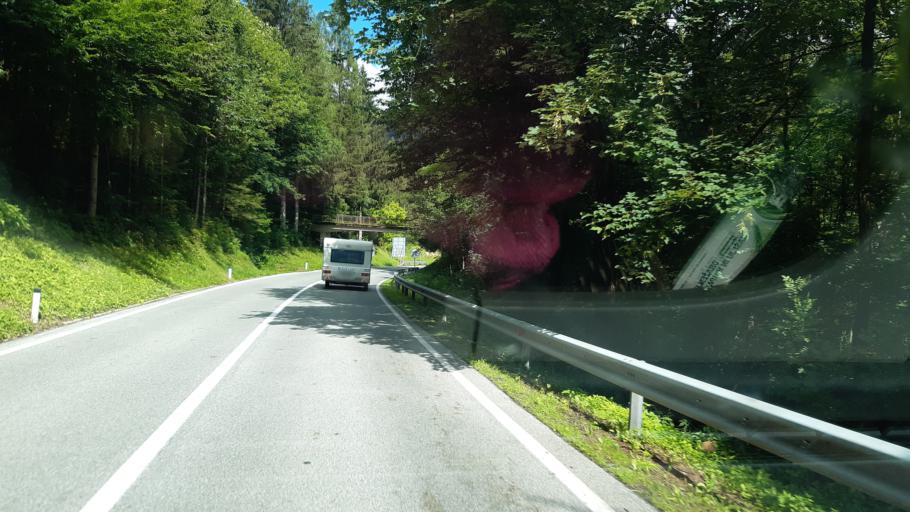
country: SI
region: Trzic
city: Trzic
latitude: 46.3690
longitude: 14.3054
